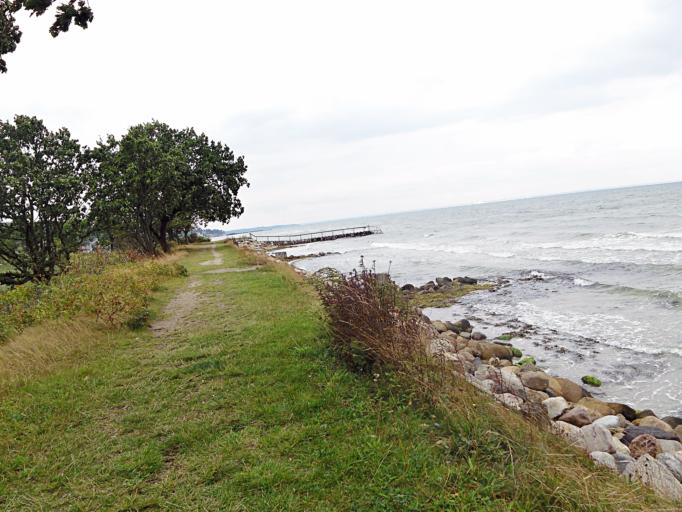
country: DK
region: Capital Region
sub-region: Fredensborg Kommune
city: Humlebaek
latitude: 55.9408
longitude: 12.5276
